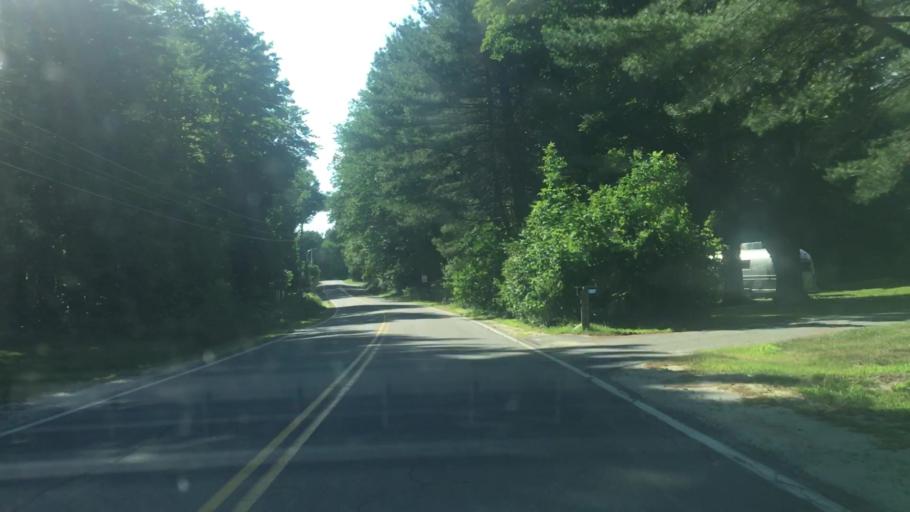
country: US
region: Maine
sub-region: York County
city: Hollis Center
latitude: 43.6339
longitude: -70.5694
